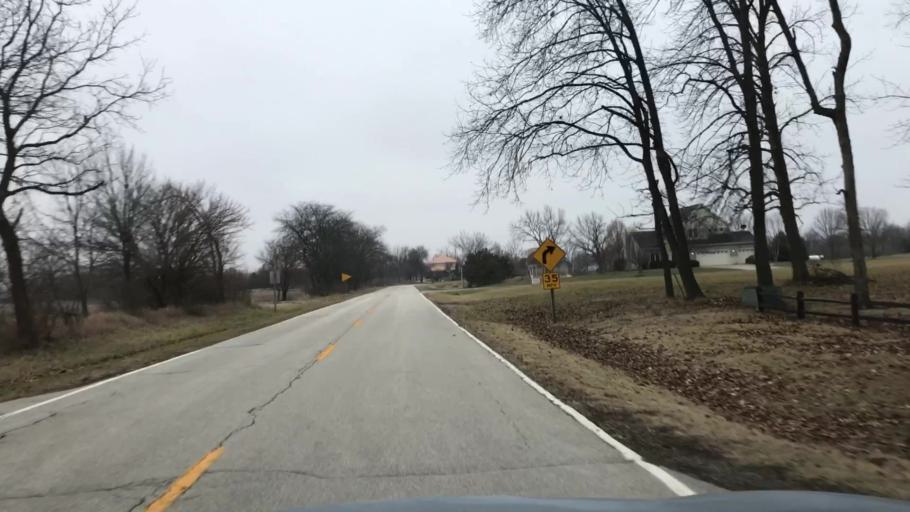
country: US
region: Illinois
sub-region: McLean County
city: Hudson
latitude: 40.6353
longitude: -88.9181
